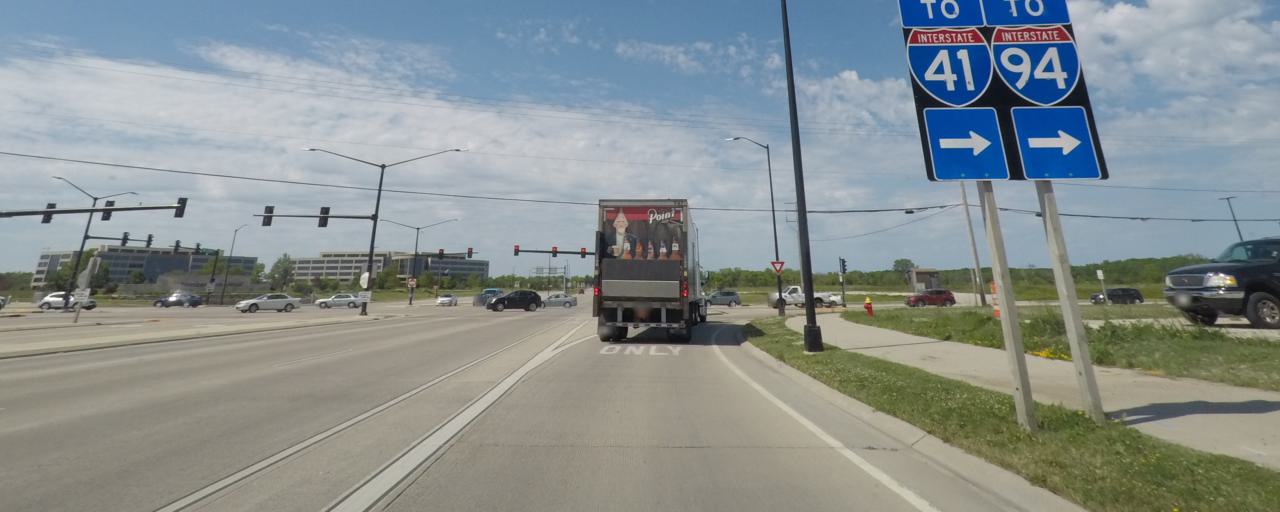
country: US
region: Wisconsin
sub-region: Milwaukee County
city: Greendale
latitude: 42.9012
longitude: -87.9502
